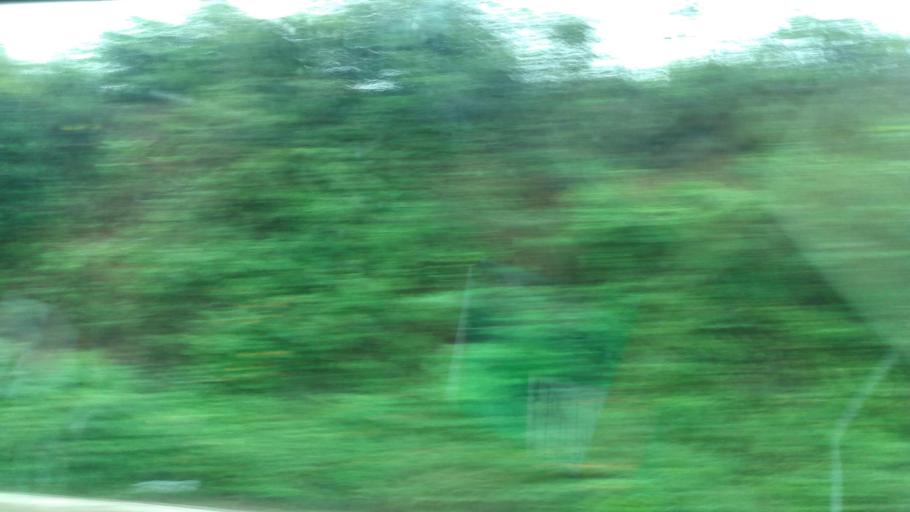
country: BR
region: Pernambuco
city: Garanhuns
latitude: -8.8752
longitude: -36.5190
